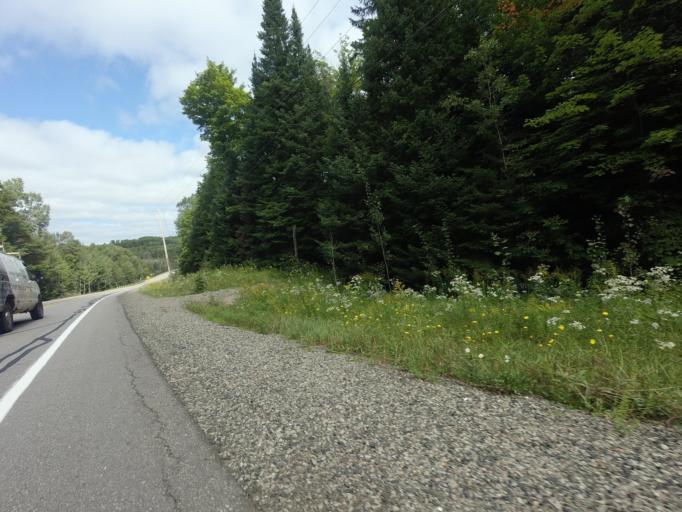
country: CA
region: Ontario
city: Bancroft
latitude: 44.9298
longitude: -78.3299
